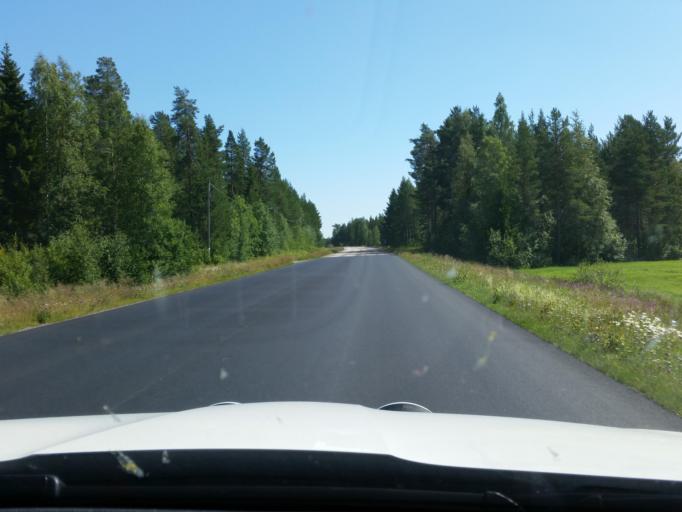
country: SE
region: Norrbotten
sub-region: Alvsbyns Kommun
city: AElvsbyn
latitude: 65.6765
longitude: 20.8300
